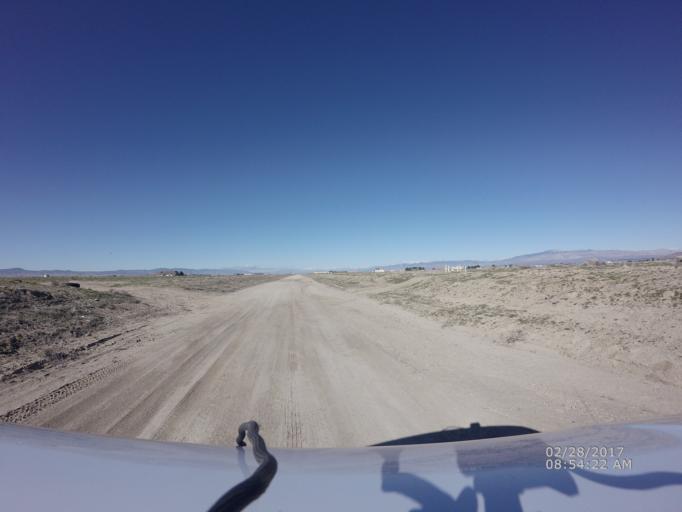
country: US
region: California
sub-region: Kern County
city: Rosamond
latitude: 34.8056
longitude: -118.2462
